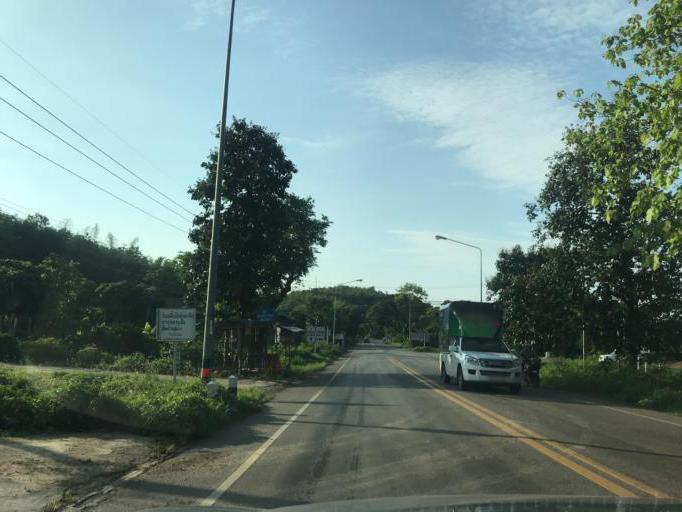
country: TH
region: Phayao
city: Phu Kam Yao
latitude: 19.3115
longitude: 100.0038
